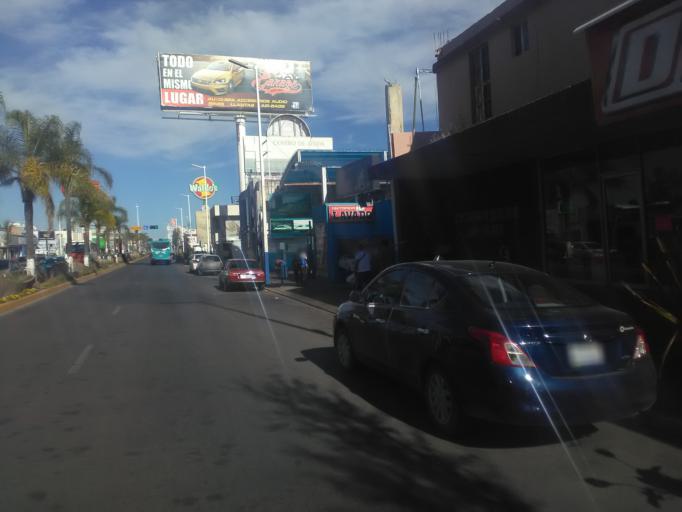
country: MX
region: Durango
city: Victoria de Durango
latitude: 24.0263
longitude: -104.6606
